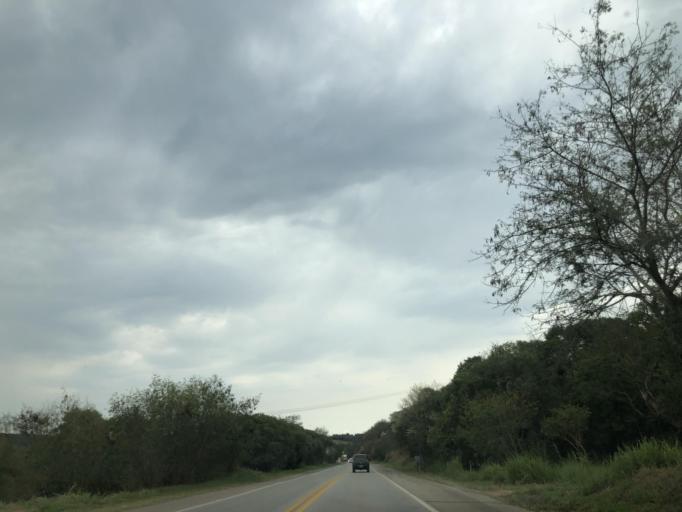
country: BR
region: Sao Paulo
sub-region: Salto De Pirapora
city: Salto de Pirapora
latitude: -23.7223
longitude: -47.6387
